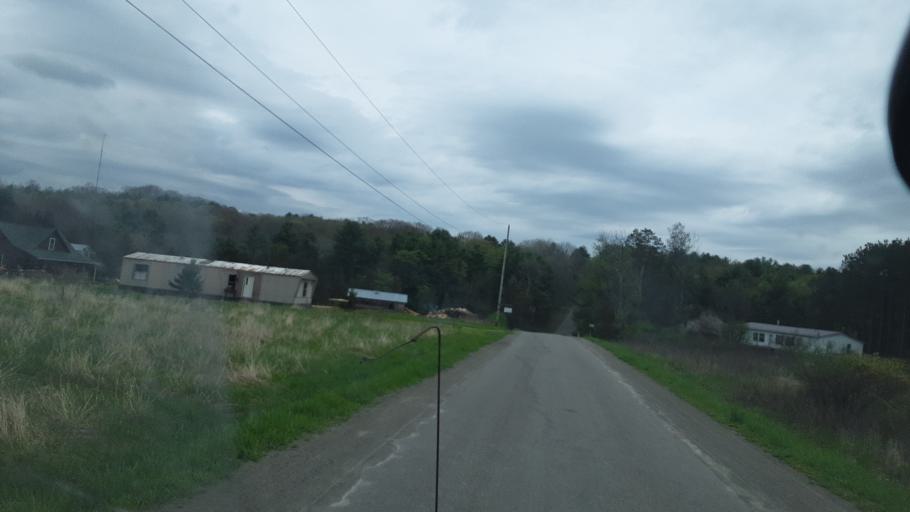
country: US
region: New York
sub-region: Steuben County
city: Addison
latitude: 42.0930
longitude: -77.3050
